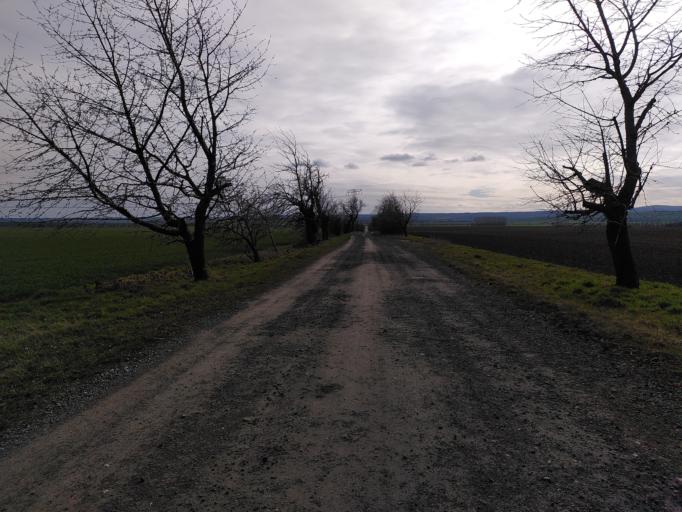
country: DE
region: Saxony-Anhalt
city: Gatersleben
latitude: 51.7970
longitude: 11.2581
